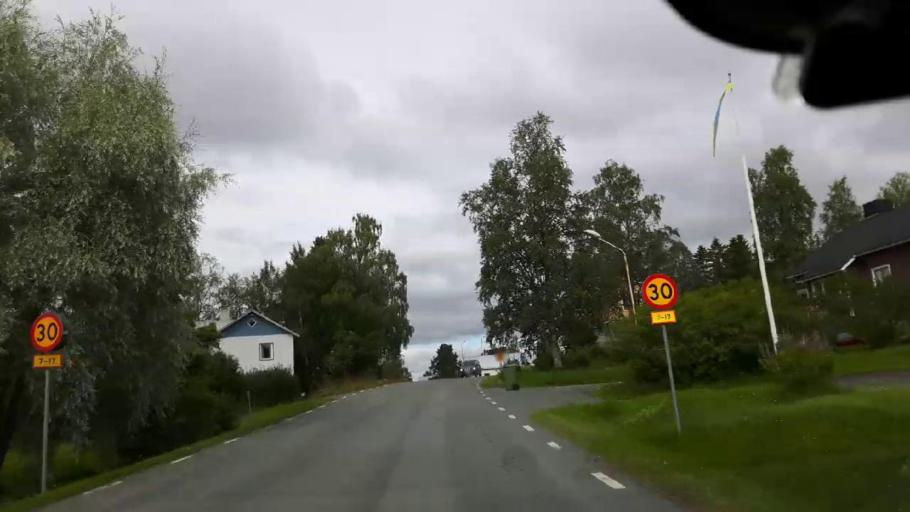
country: SE
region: Jaemtland
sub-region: Krokoms Kommun
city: Valla
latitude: 63.4941
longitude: 13.9011
